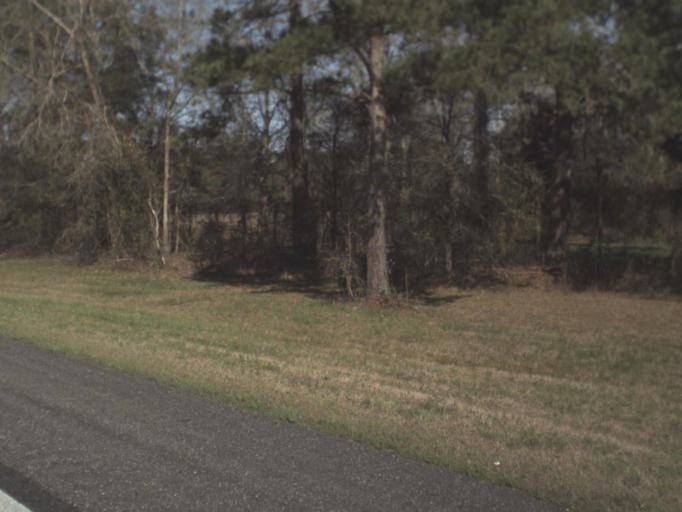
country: US
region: Florida
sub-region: Jefferson County
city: Monticello
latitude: 30.4787
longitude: -83.9288
